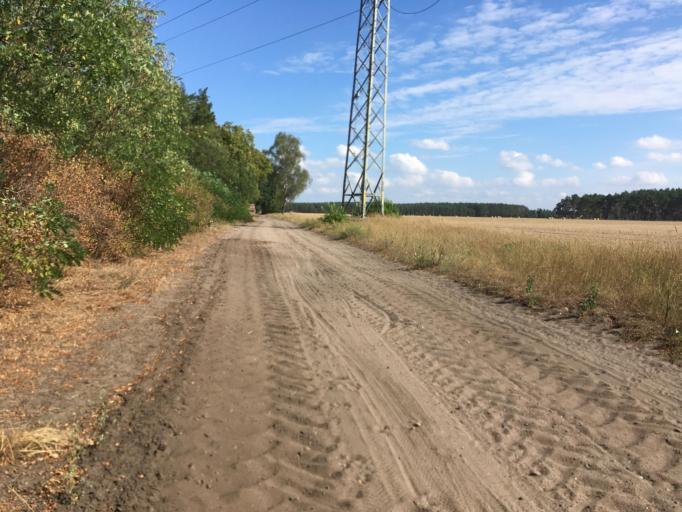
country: DE
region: Brandenburg
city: Zehdenick
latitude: 52.9578
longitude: 13.3823
